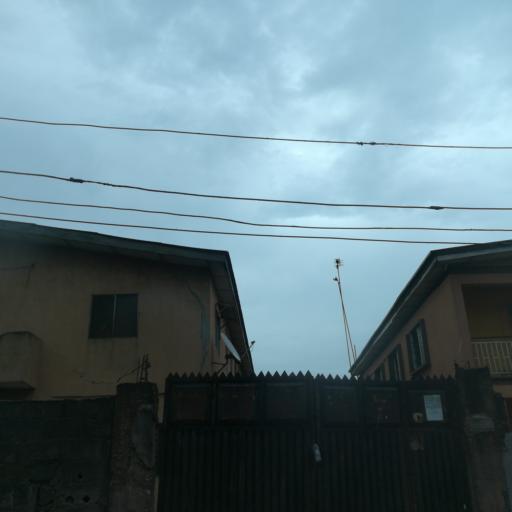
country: NG
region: Lagos
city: Oshodi
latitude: 6.5552
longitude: 3.3456
